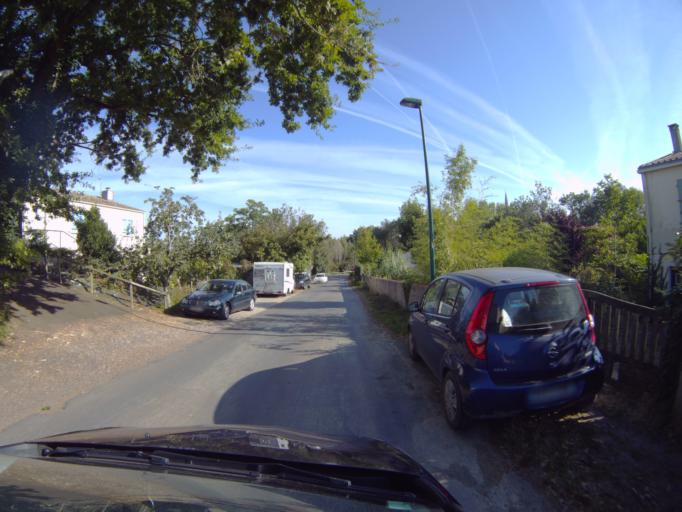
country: FR
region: Pays de la Loire
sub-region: Departement de la Vendee
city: Saint-Hilaire-de-Talmont
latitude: 46.4676
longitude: -1.6048
